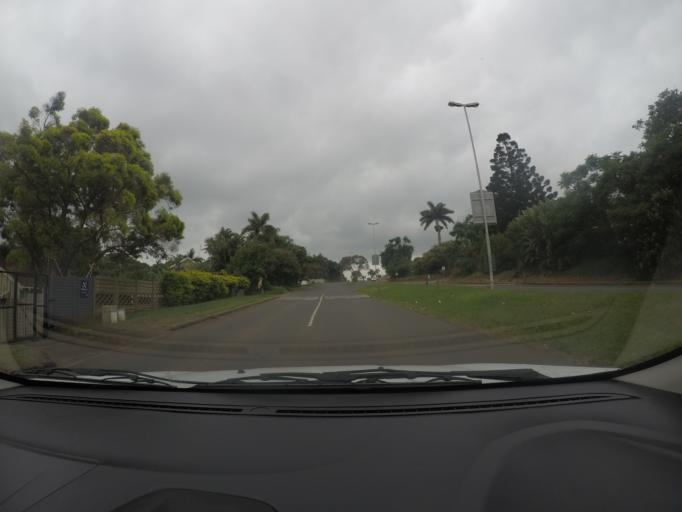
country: ZA
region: KwaZulu-Natal
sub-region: uThungulu District Municipality
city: Empangeni
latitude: -28.7670
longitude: 31.8951
